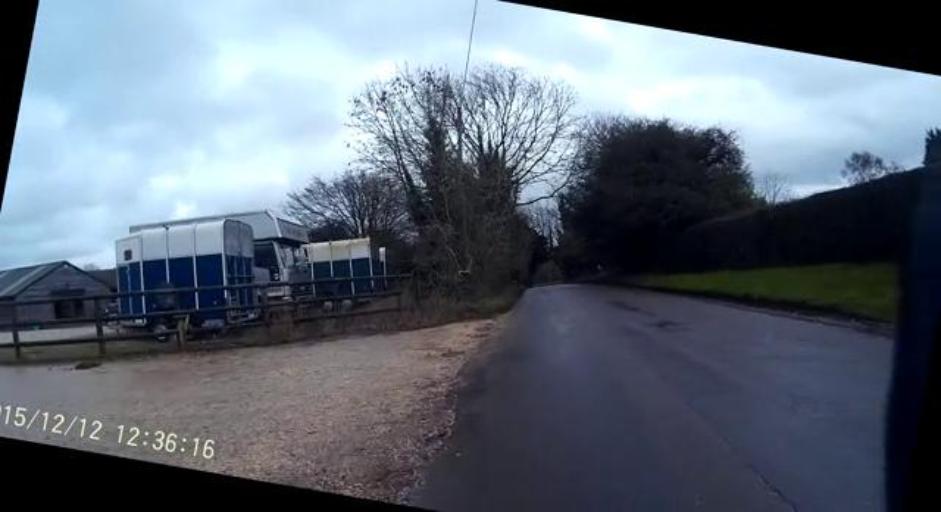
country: GB
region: England
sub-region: Hampshire
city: Cowplain
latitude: 50.9528
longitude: -0.9827
